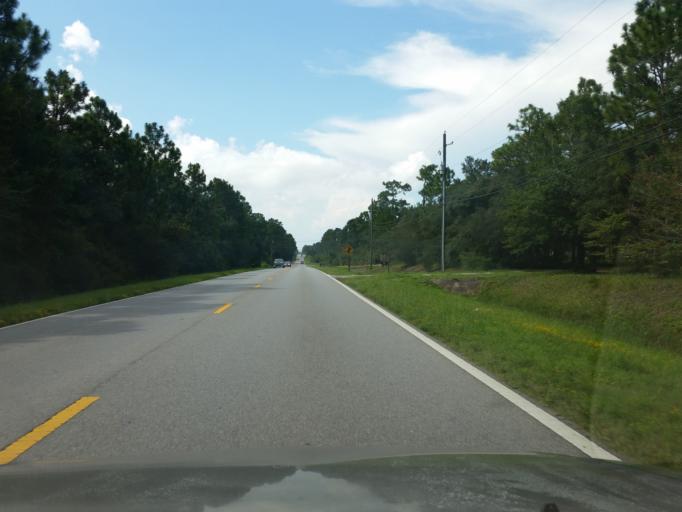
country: US
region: Florida
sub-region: Escambia County
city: Myrtle Grove
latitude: 30.3572
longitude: -87.4028
